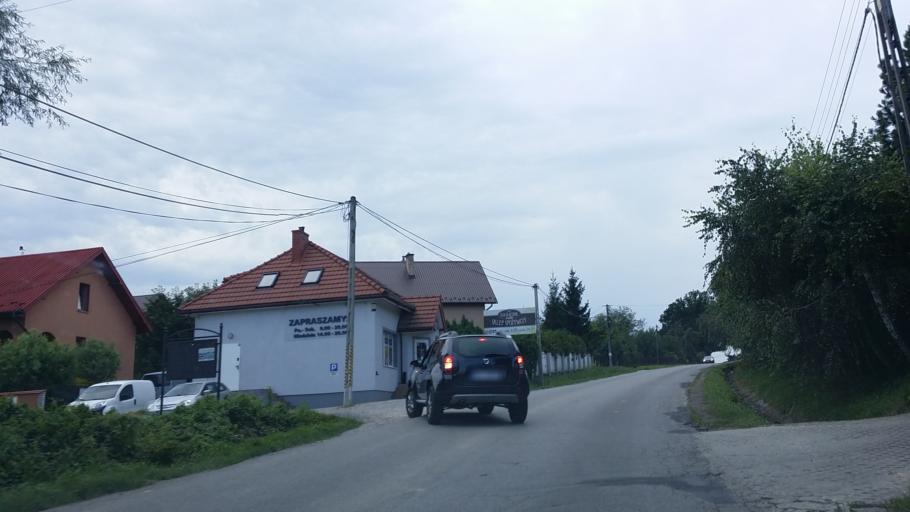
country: PL
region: Lesser Poland Voivodeship
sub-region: Powiat wielicki
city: Pawlikowice
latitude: 49.9739
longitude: 20.0259
